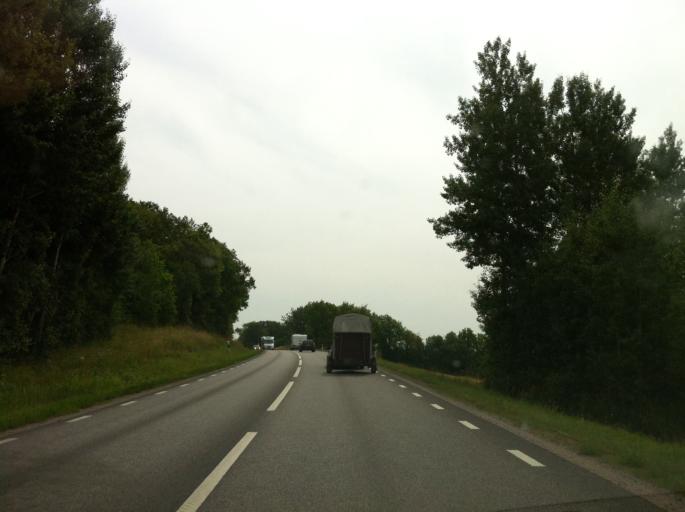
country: SE
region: Blekinge
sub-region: Karlskrona Kommun
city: Sturko
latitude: 56.1948
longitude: 15.6982
